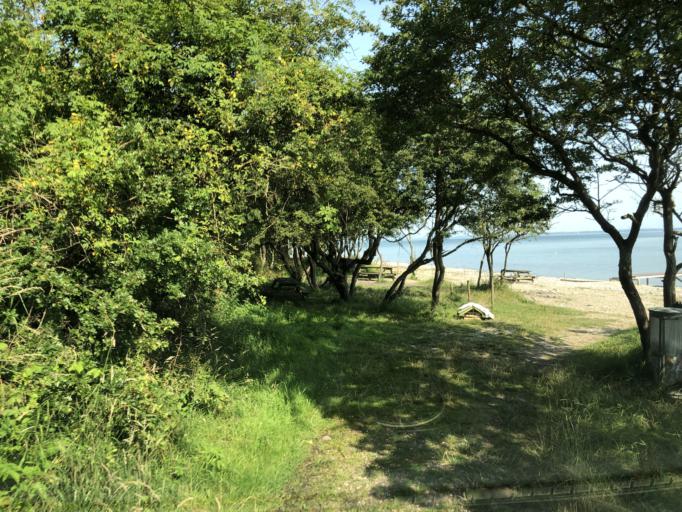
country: DK
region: Central Jutland
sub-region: Lemvig Kommune
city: Lemvig
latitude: 56.5688
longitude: 8.4280
